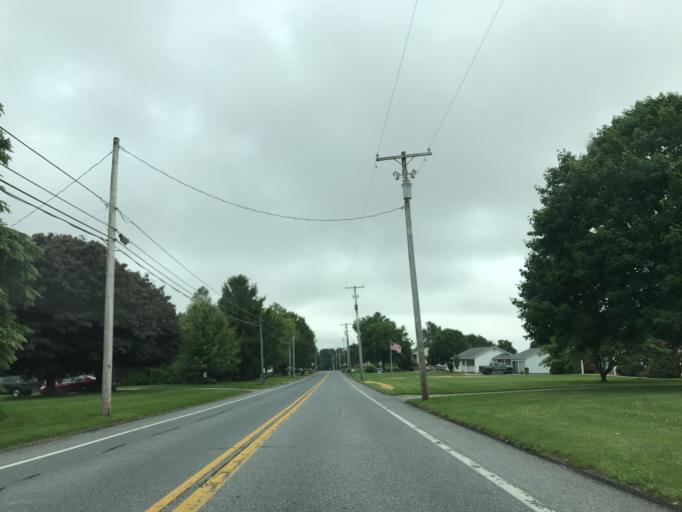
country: US
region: Pennsylvania
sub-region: York County
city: Stewartstown
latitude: 39.8045
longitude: -76.5969
